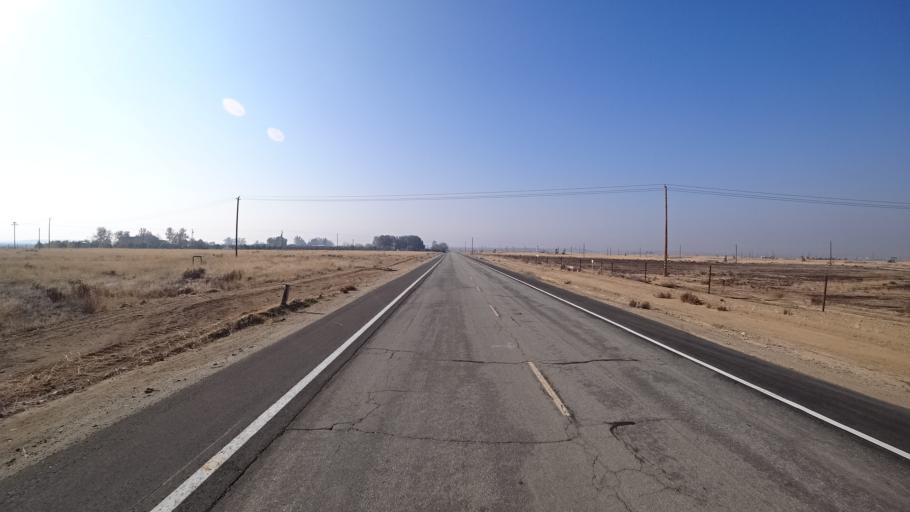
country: US
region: California
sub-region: Kern County
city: Lamont
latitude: 35.3709
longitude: -118.8496
